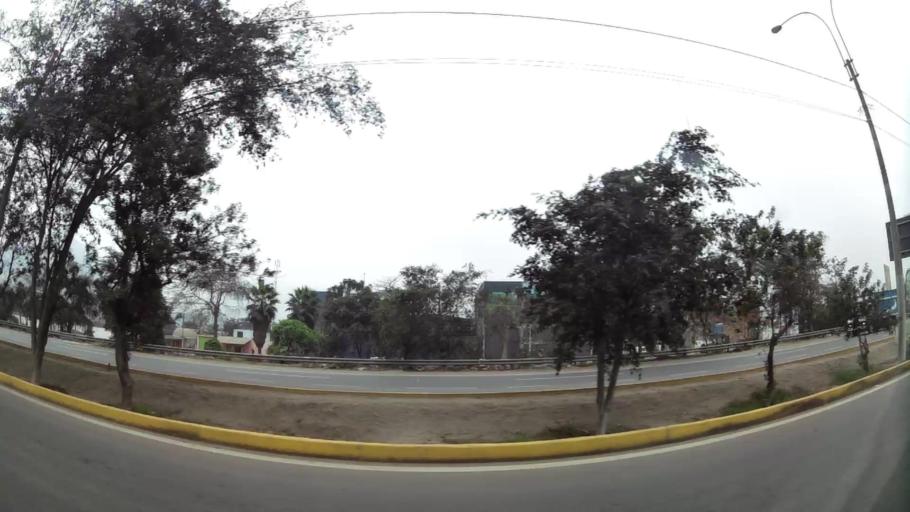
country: PE
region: Lima
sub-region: Lima
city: Vitarte
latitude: -12.0198
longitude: -76.9454
